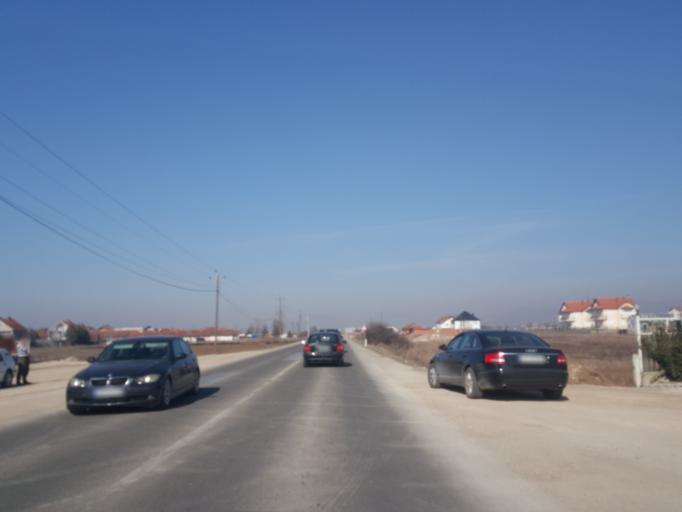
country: XK
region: Mitrovica
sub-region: Vushtrri
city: Vushtrri
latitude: 42.7846
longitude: 21.0099
